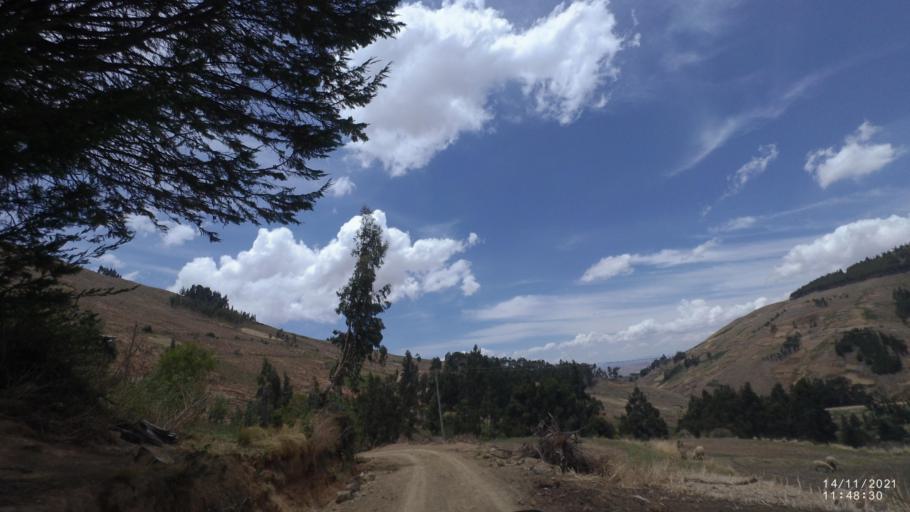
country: BO
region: Cochabamba
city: Colomi
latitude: -17.3549
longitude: -65.9835
